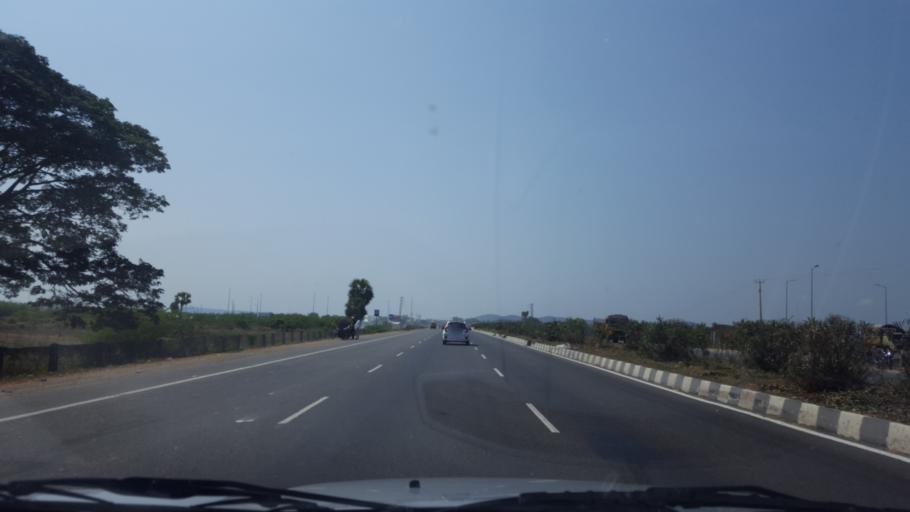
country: IN
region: Andhra Pradesh
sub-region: Guntur
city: Chilakalurupet
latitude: 16.0105
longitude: 80.1172
